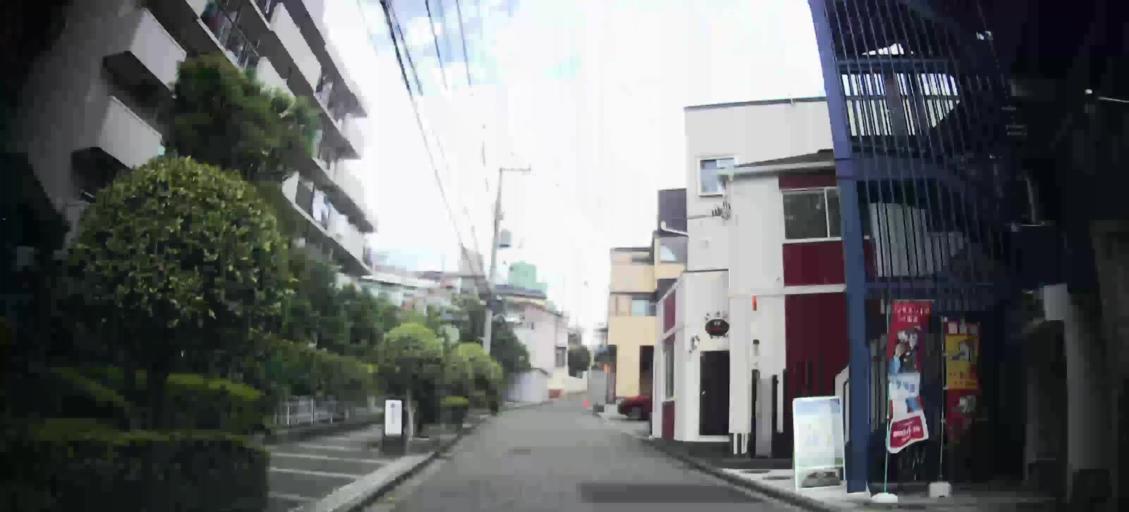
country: JP
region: Kanagawa
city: Minami-rinkan
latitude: 35.4775
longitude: 139.5481
